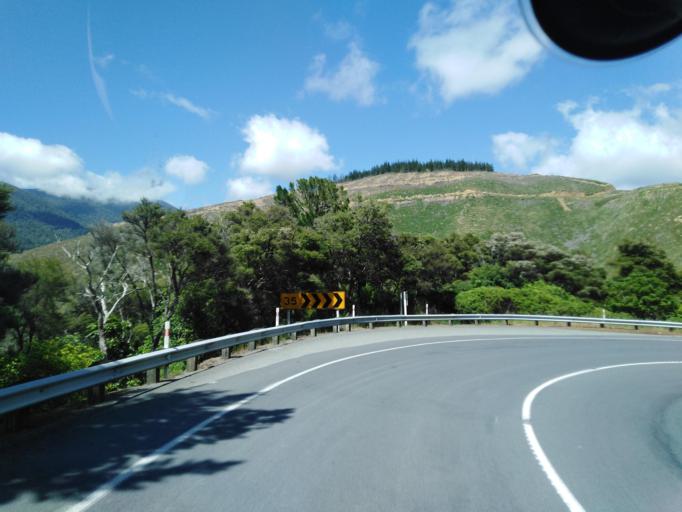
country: NZ
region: Nelson
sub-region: Nelson City
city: Nelson
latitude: -41.2290
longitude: 173.4242
